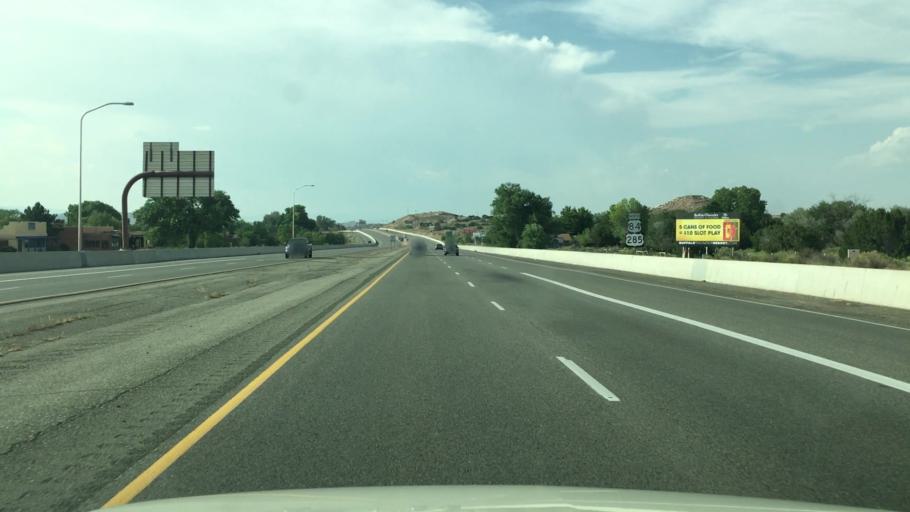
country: US
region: New Mexico
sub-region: Santa Fe County
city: Nambe
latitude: 35.8623
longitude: -106.0004
